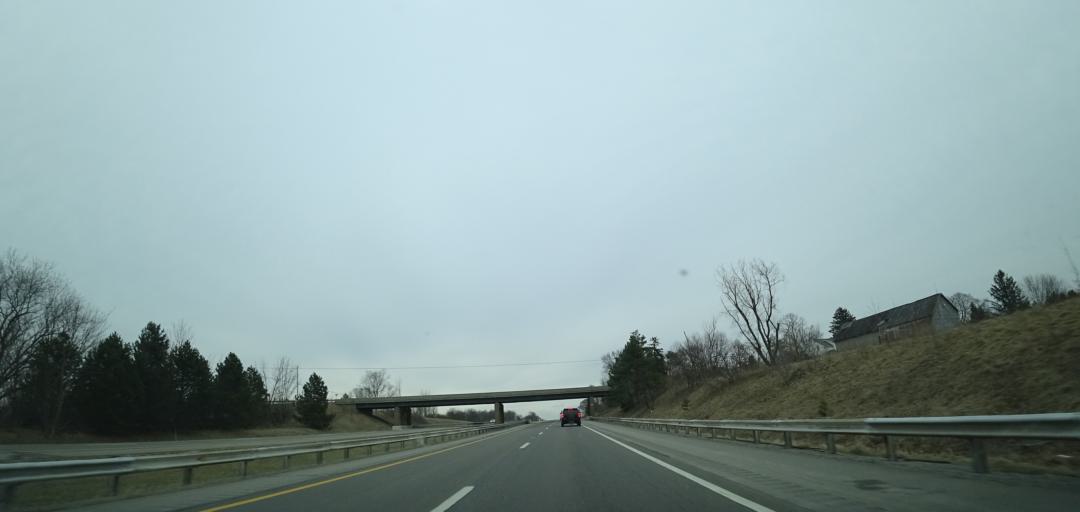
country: US
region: Ohio
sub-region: Mahoning County
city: New Middletown
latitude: 40.9445
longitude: -80.6165
